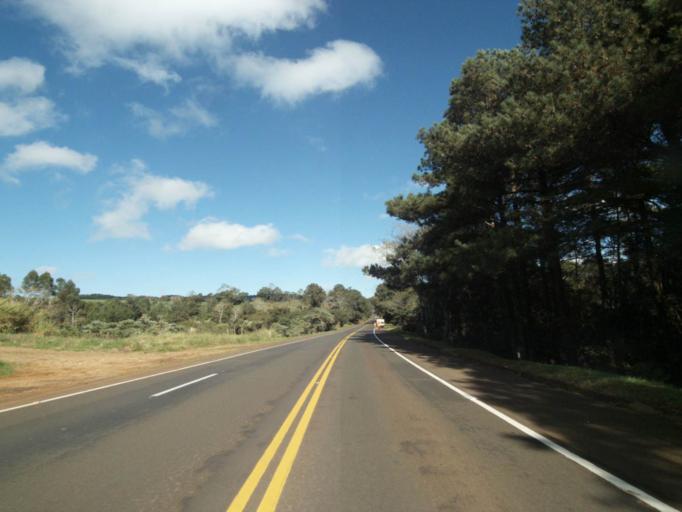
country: BR
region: Parana
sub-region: Faxinal
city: Faxinal
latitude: -23.8823
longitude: -51.1746
